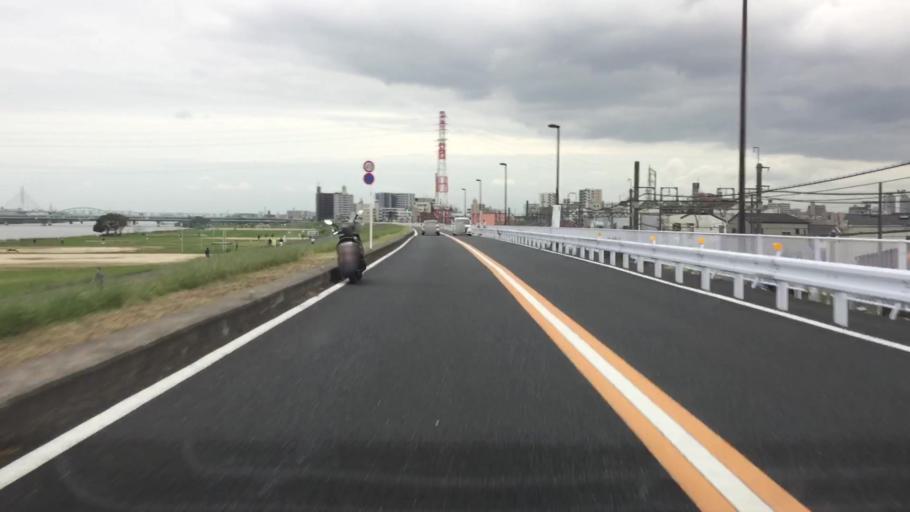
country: JP
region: Saitama
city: Soka
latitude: 35.7389
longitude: 139.8202
